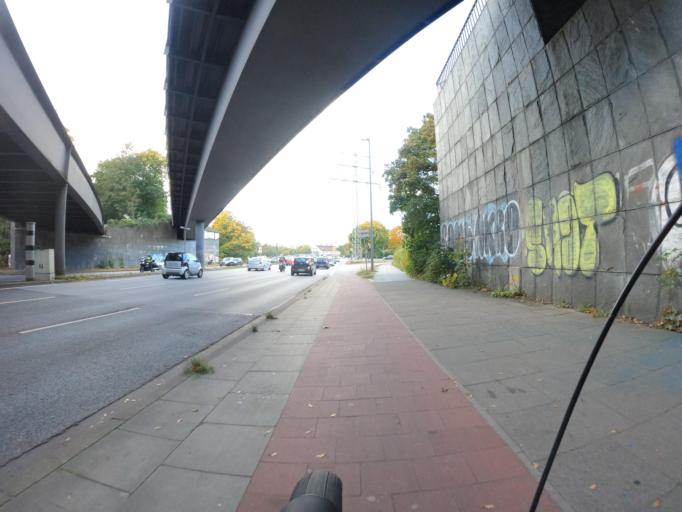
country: DE
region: Hamburg
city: Winterhude
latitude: 53.6023
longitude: 9.9965
